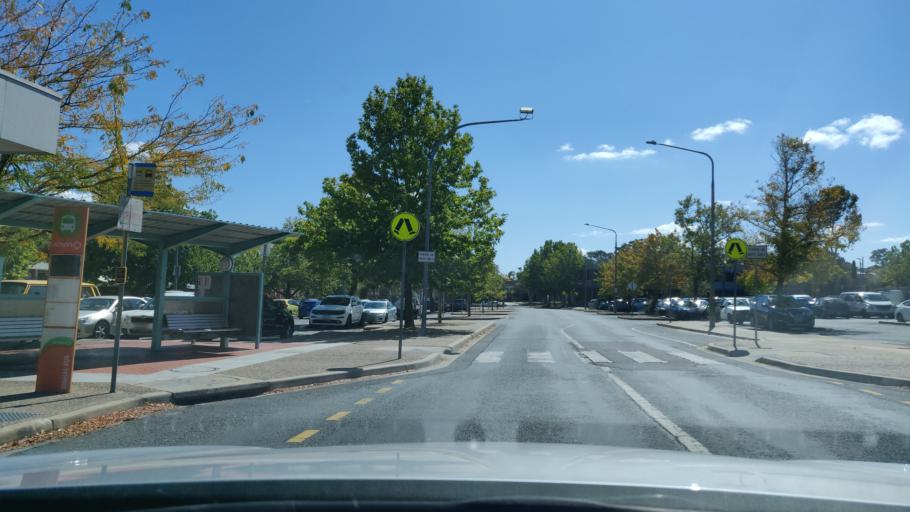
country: AU
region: Australian Capital Territory
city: Macarthur
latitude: -35.3656
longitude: 149.0953
